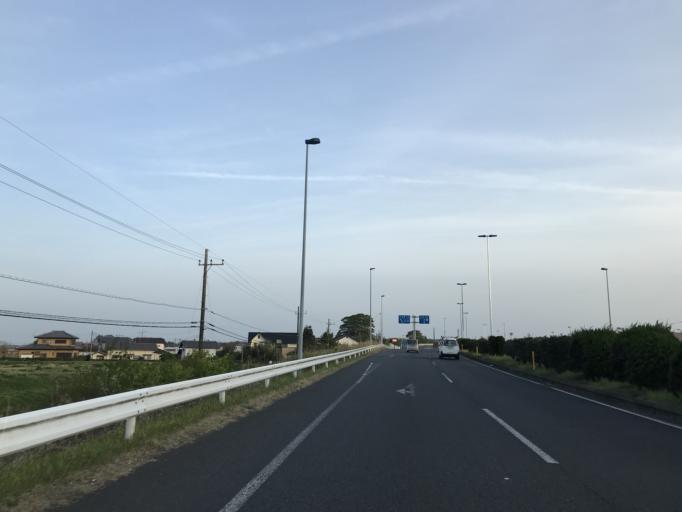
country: JP
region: Ibaraki
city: Katsuta
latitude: 36.3644
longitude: 140.5027
